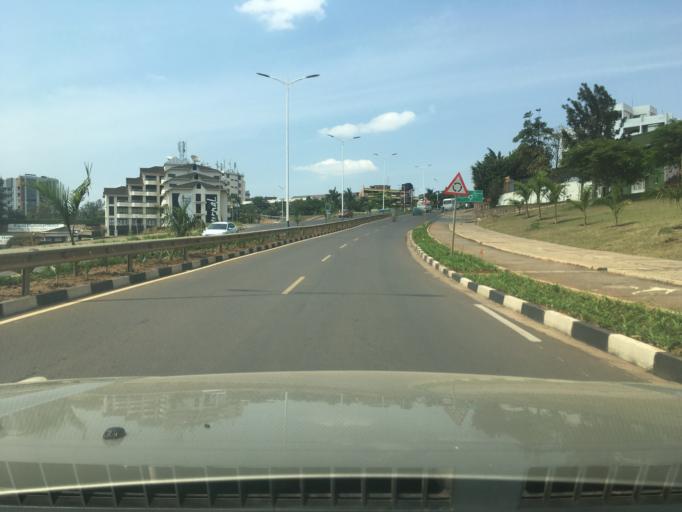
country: RW
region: Kigali
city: Kigali
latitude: -1.9526
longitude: 30.0949
